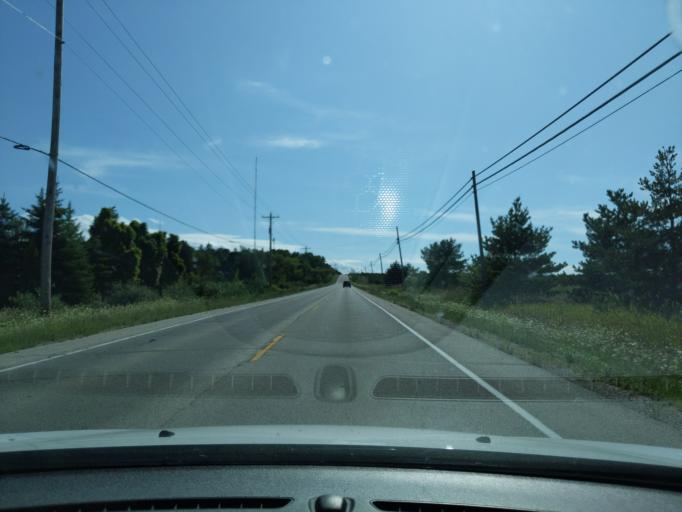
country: US
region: Wisconsin
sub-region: Door County
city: Sturgeon Bay
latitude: 45.2438
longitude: -87.0876
